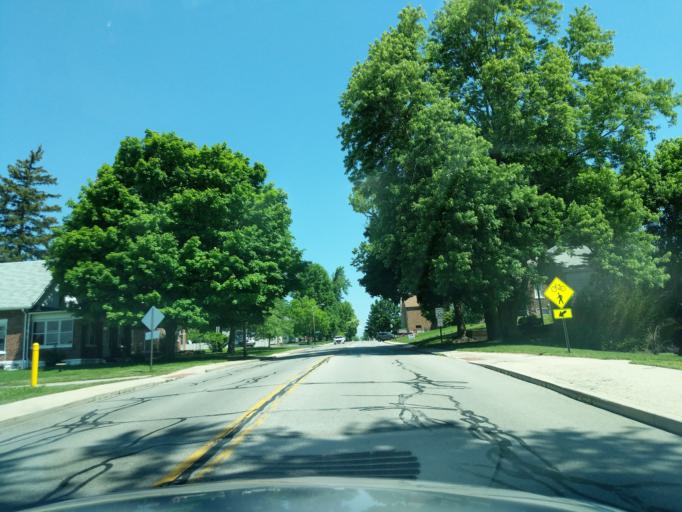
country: US
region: Indiana
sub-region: Whitley County
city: Columbia City
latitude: 41.1528
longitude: -85.4912
